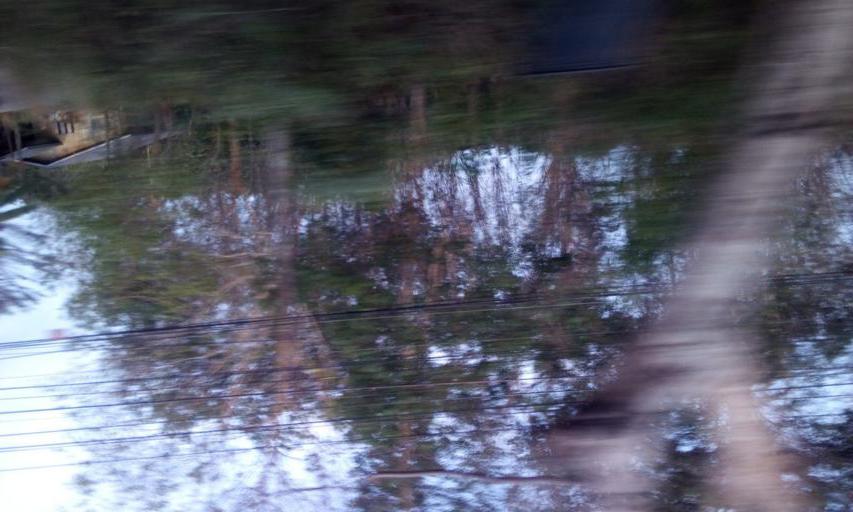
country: TH
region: Trat
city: Laem Ngop
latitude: 12.2459
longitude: 102.2938
